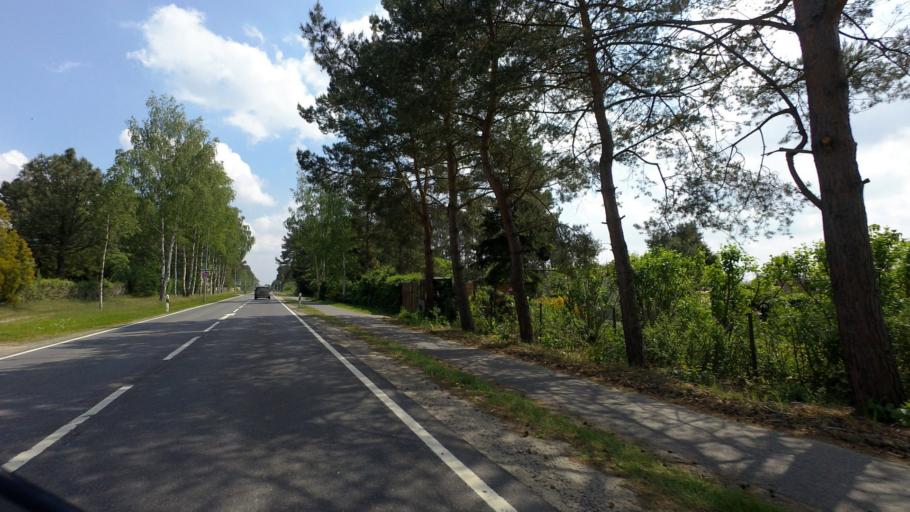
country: DE
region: Saxony
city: Weisswasser
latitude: 51.4940
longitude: 14.6504
